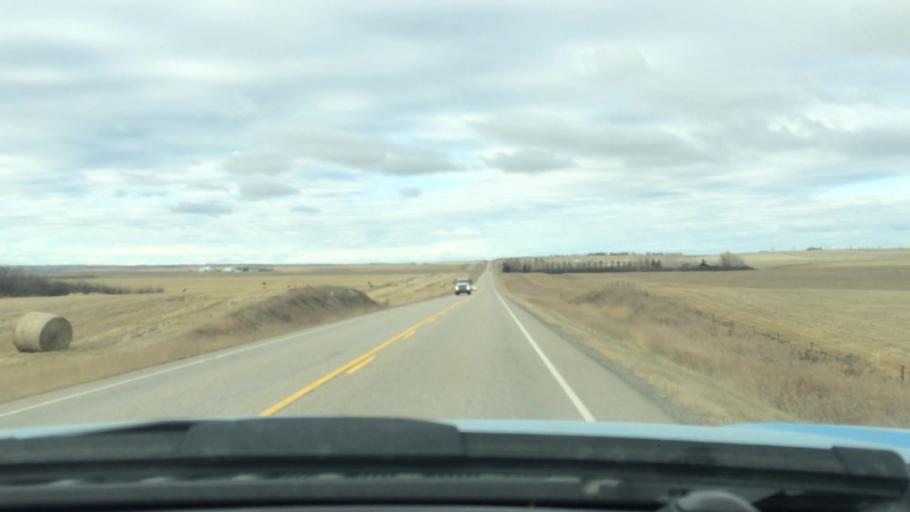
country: CA
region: Alberta
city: Airdrie
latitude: 51.2125
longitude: -114.0801
